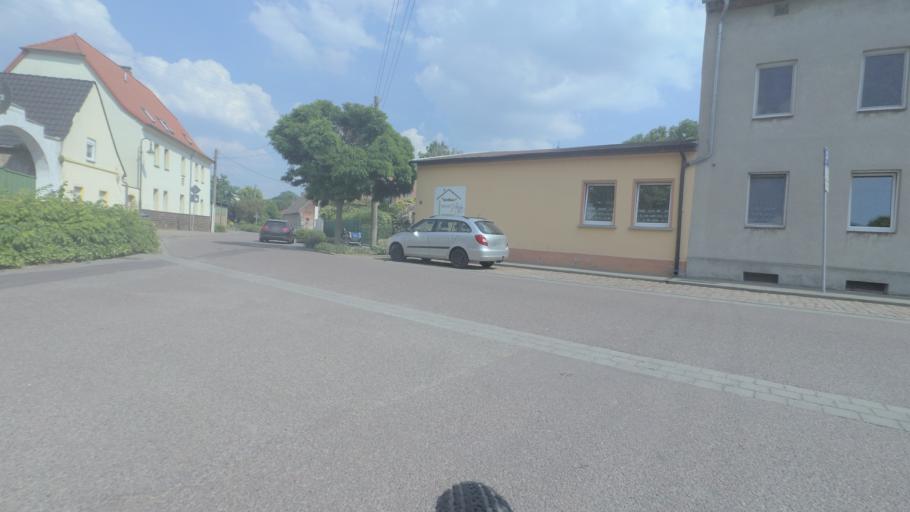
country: DE
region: Saxony-Anhalt
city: Koethen
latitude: 51.7616
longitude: 11.9339
